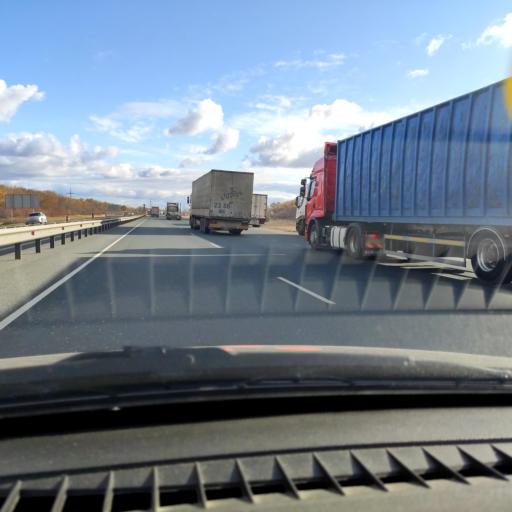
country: RU
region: Samara
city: Varlamovo
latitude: 53.1962
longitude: 48.2995
